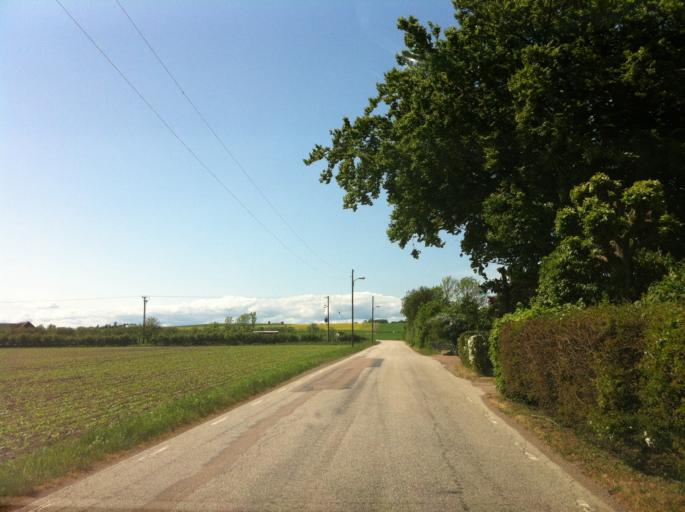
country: SE
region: Skane
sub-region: Landskrona
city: Asmundtorp
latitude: 55.9241
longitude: 12.9354
